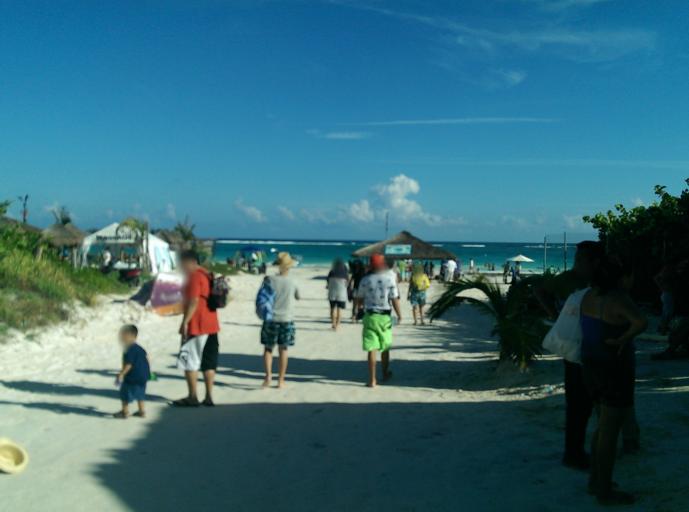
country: MX
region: Quintana Roo
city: Tulum
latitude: 20.2030
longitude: -87.4327
